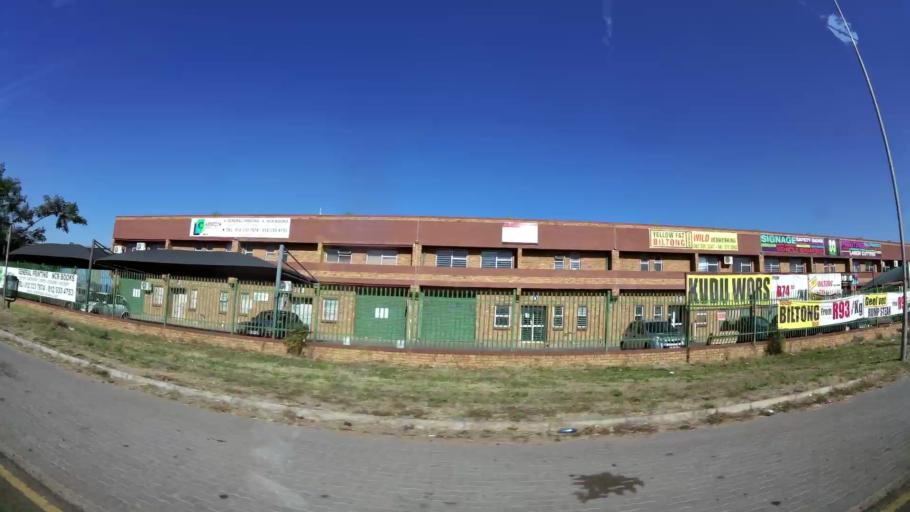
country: ZA
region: Gauteng
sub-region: City of Tshwane Metropolitan Municipality
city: Pretoria
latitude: -25.7170
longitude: 28.2463
